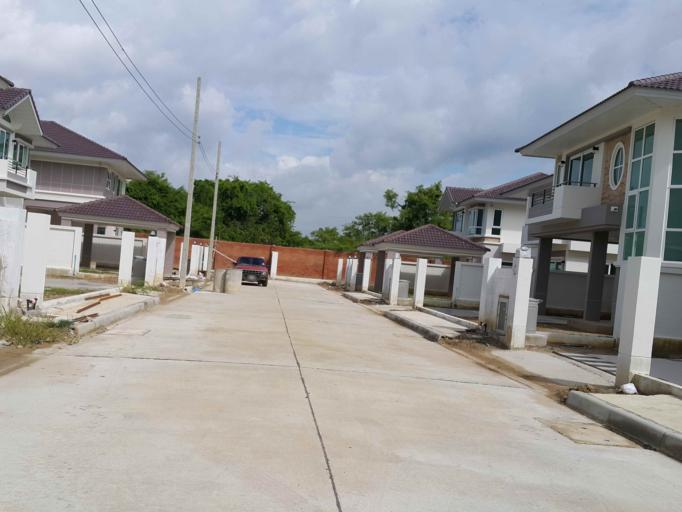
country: TH
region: Chiang Mai
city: Saraphi
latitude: 18.7579
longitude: 99.0651
